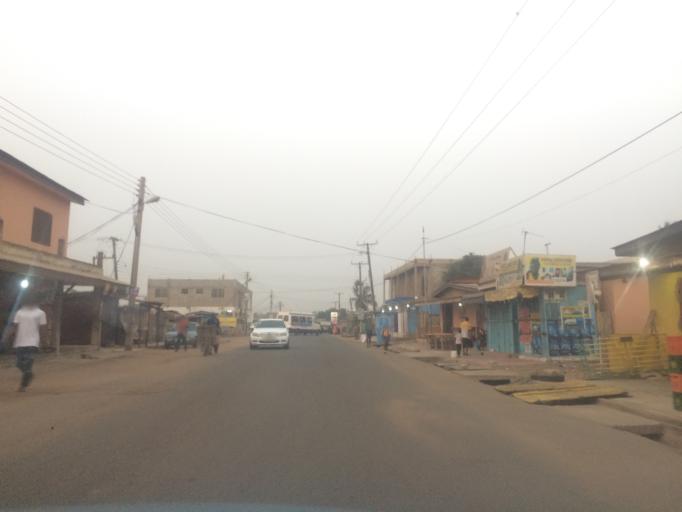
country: GH
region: Greater Accra
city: Teshi Old Town
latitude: 5.5905
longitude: -0.1107
